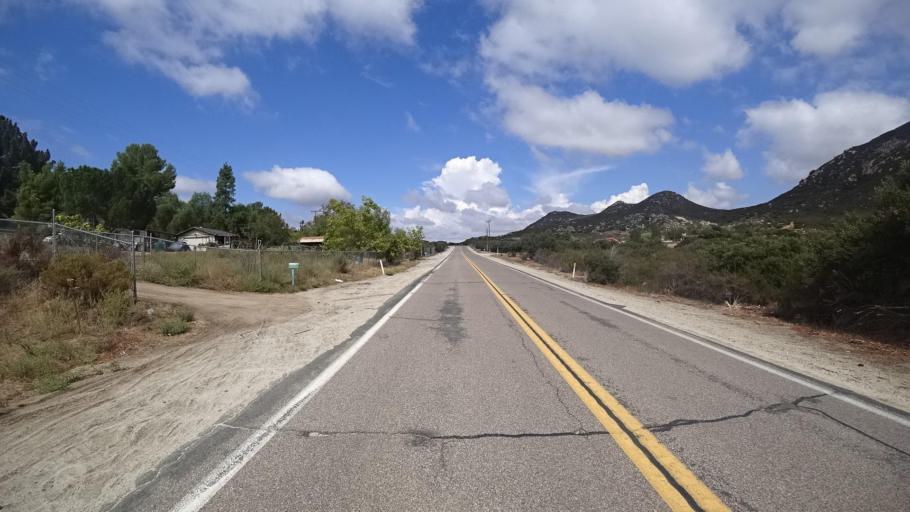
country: US
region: California
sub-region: San Diego County
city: Campo
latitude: 32.6831
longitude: -116.4888
